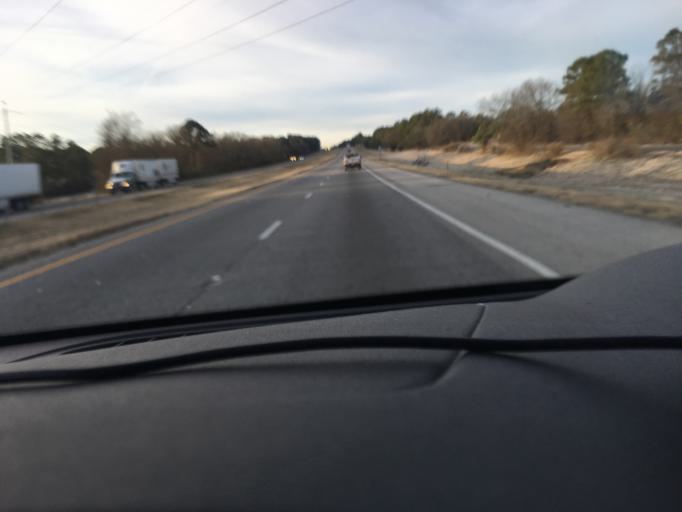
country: US
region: Arkansas
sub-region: Hot Spring County
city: Malvern
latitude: 34.3286
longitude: -92.9243
